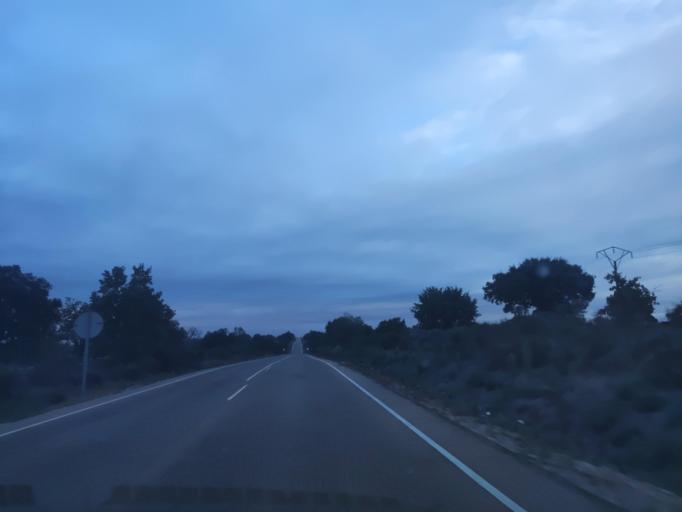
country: ES
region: Castille and Leon
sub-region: Provincia de Salamanca
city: Lumbrales
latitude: 40.9014
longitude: -6.7158
